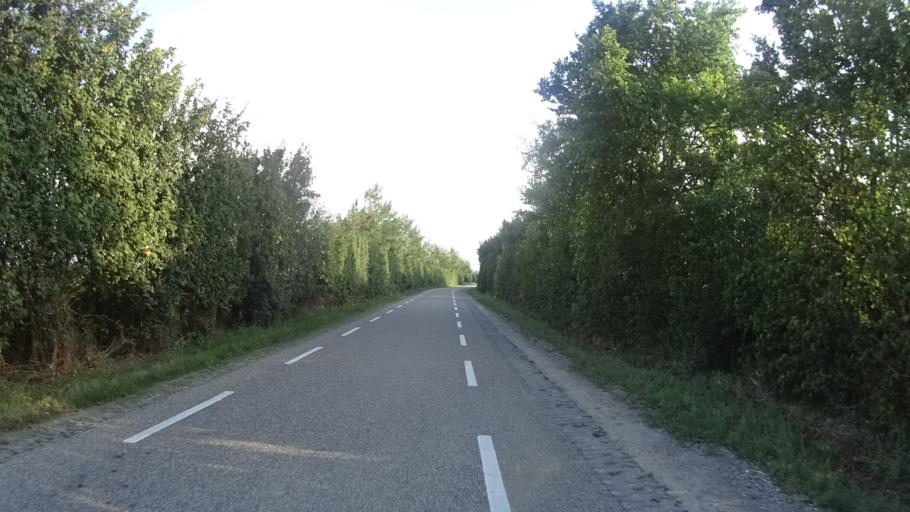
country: NL
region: Zeeland
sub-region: Gemeente Middelburg
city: Middelburg
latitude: 51.5309
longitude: 3.6290
